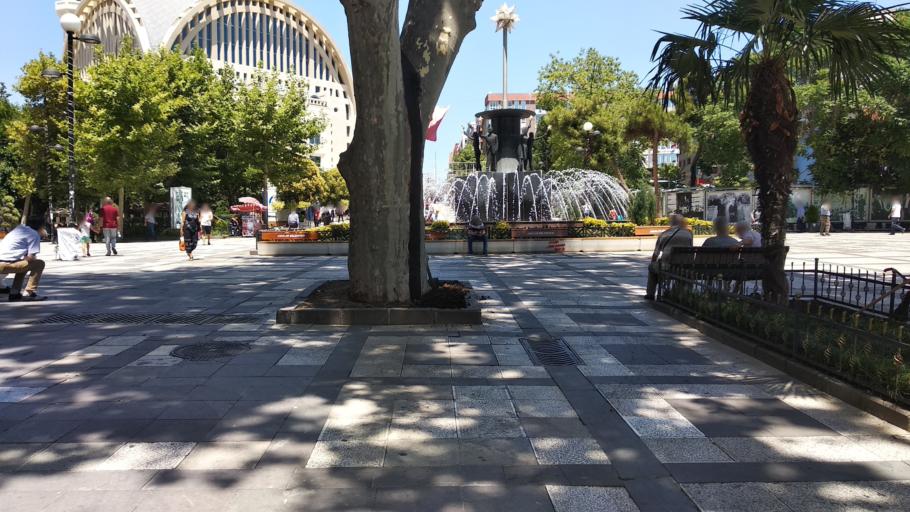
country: TR
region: Istanbul
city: Yakuplu
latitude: 40.9788
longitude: 28.7212
